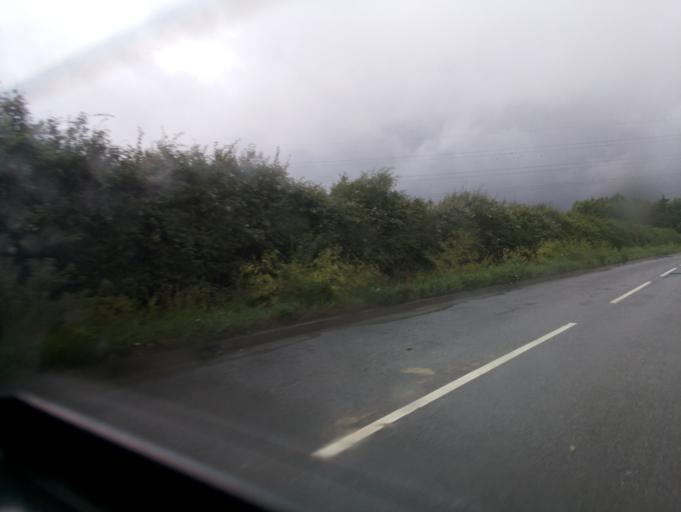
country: GB
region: England
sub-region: Gloucestershire
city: Uckington
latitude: 51.9589
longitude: -2.1338
